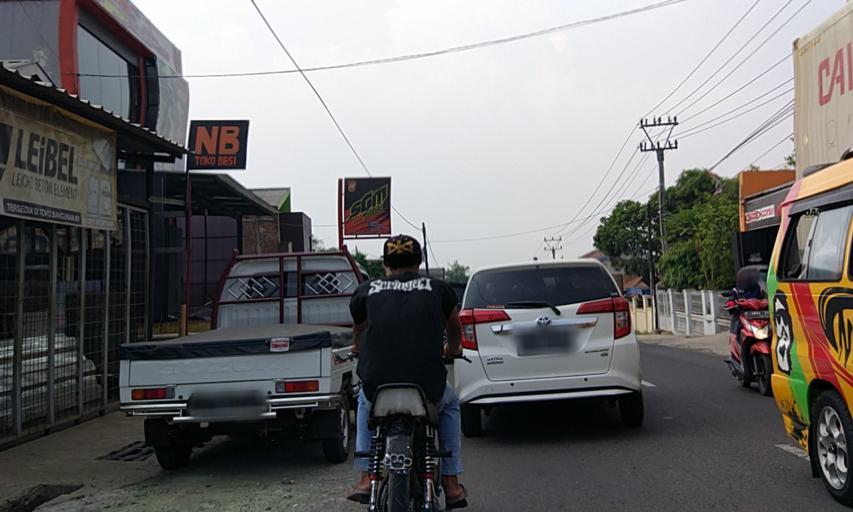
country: ID
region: West Java
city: Banjaran
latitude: -7.0598
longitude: 107.5679
